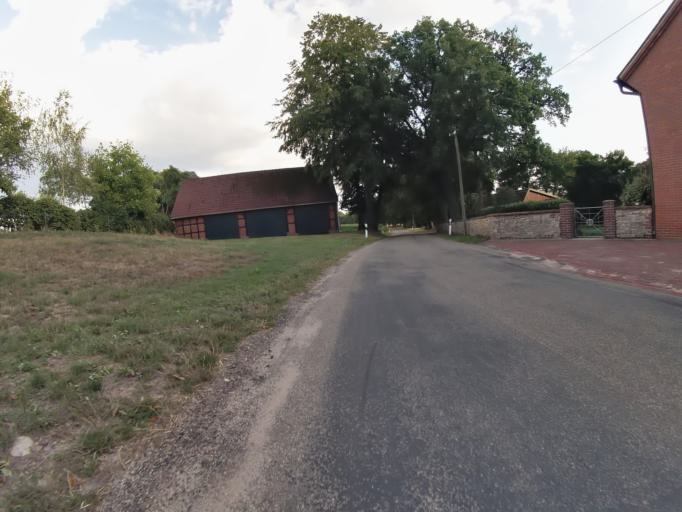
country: DE
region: North Rhine-Westphalia
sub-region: Regierungsbezirk Munster
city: Westerkappeln
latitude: 52.3651
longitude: 7.8785
